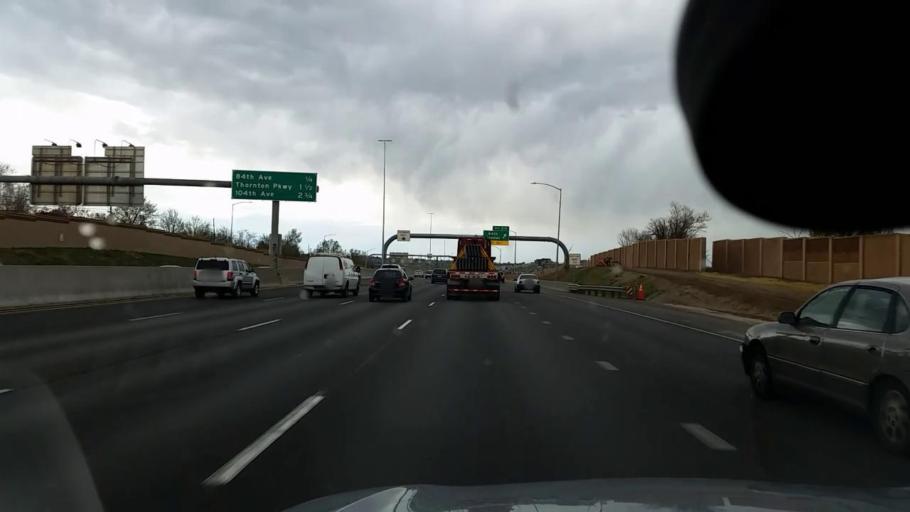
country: US
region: Colorado
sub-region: Adams County
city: Federal Heights
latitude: 39.8421
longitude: -104.9840
